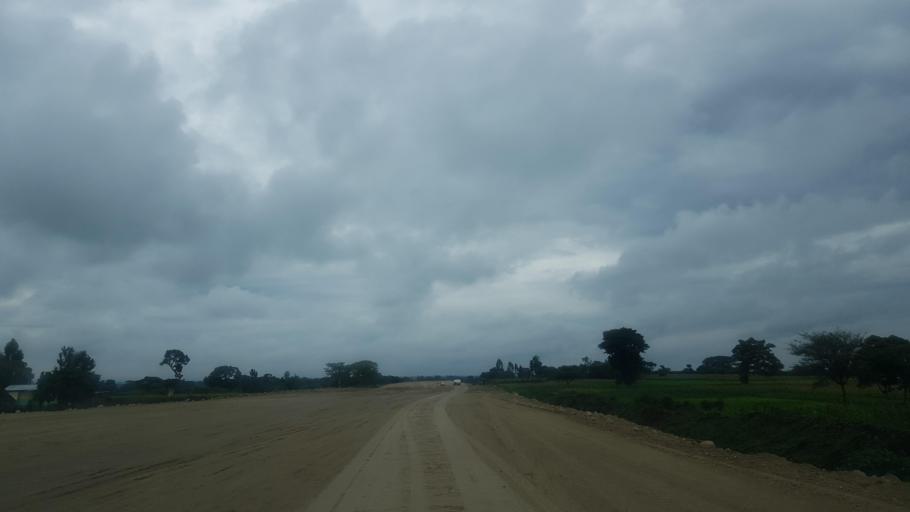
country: ET
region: Oromiya
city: Shashemene
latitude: 7.3272
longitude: 38.6330
